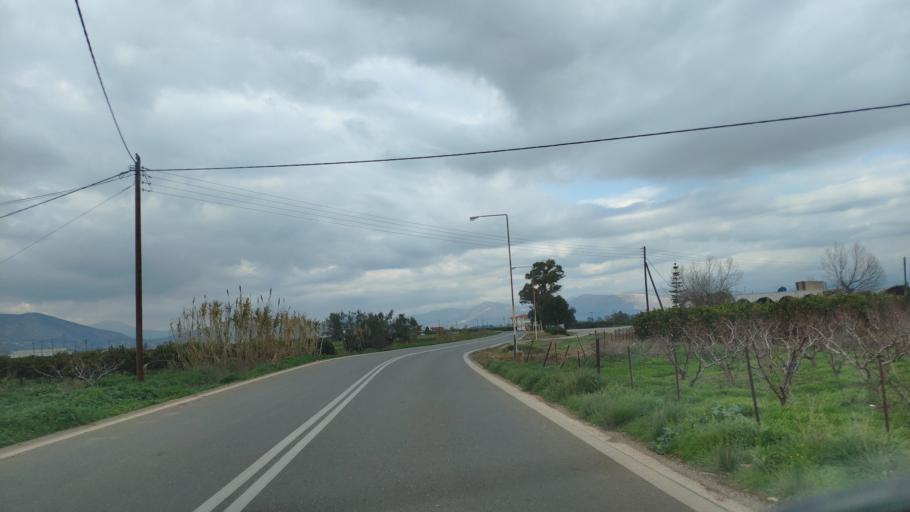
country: GR
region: Peloponnese
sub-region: Nomos Argolidos
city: Nea Kios
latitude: 37.5638
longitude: 22.7097
